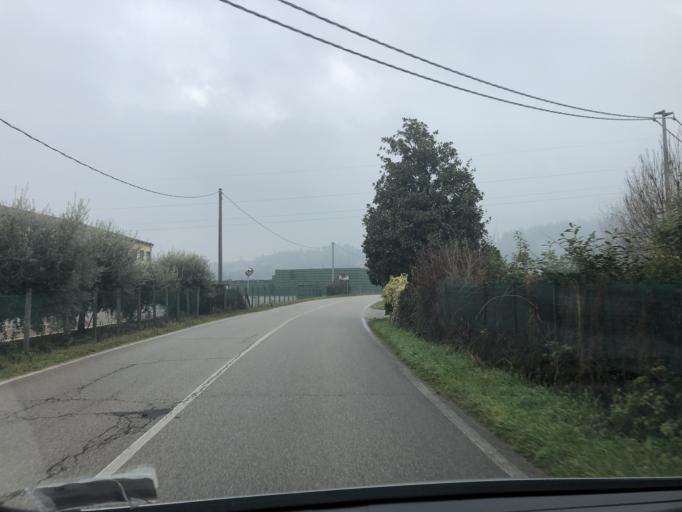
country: IT
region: Veneto
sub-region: Provincia di Verona
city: Sona
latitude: 45.4432
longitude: 10.8377
